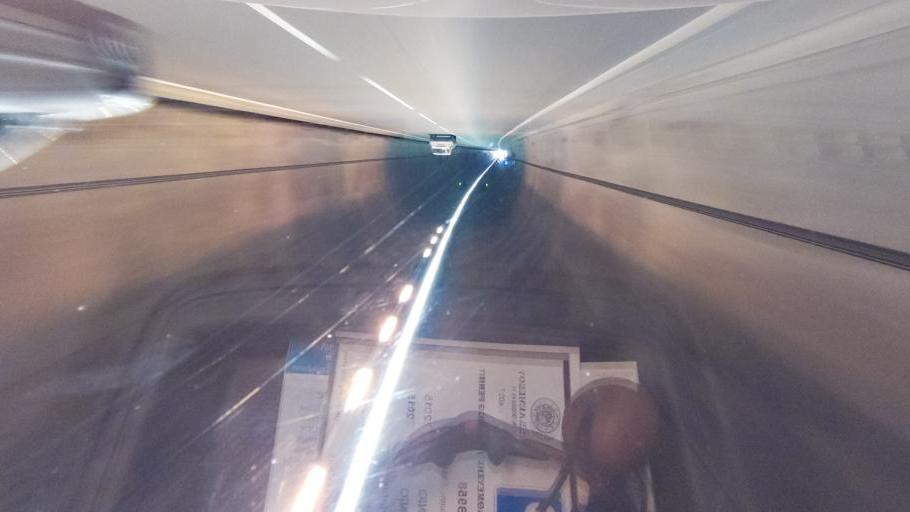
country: CY
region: Limassol
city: Sotira
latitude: 34.6969
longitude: 32.8347
